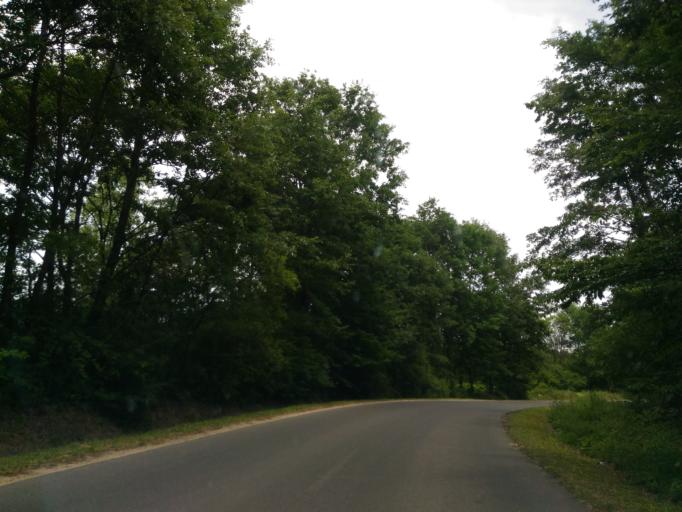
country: HU
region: Baranya
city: Komlo
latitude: 46.1822
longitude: 18.2332
